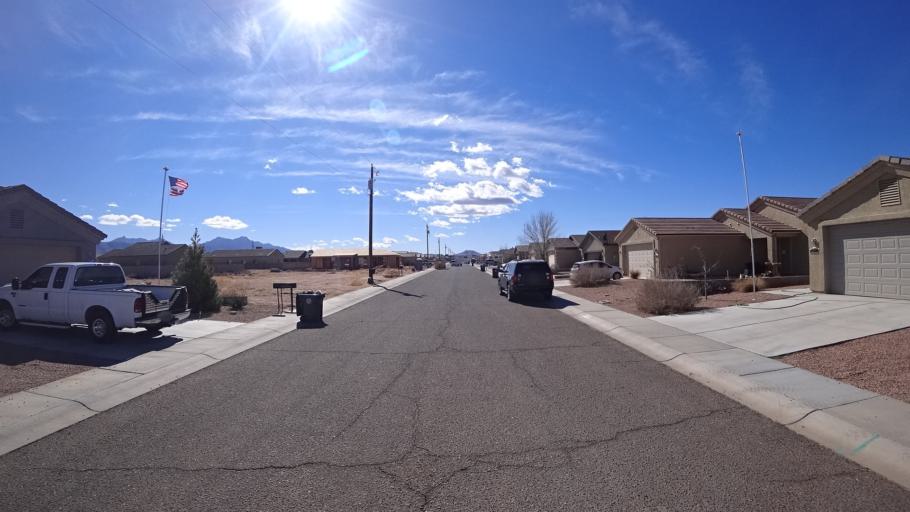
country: US
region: Arizona
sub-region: Mohave County
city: New Kingman-Butler
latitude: 35.2312
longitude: -114.0217
